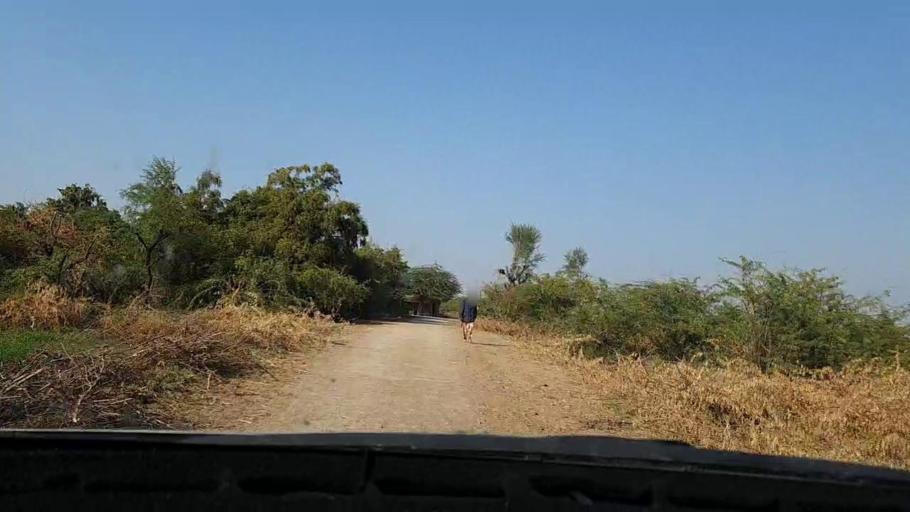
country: PK
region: Sindh
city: Tando Mittha Khan
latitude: 25.8185
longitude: 69.3154
